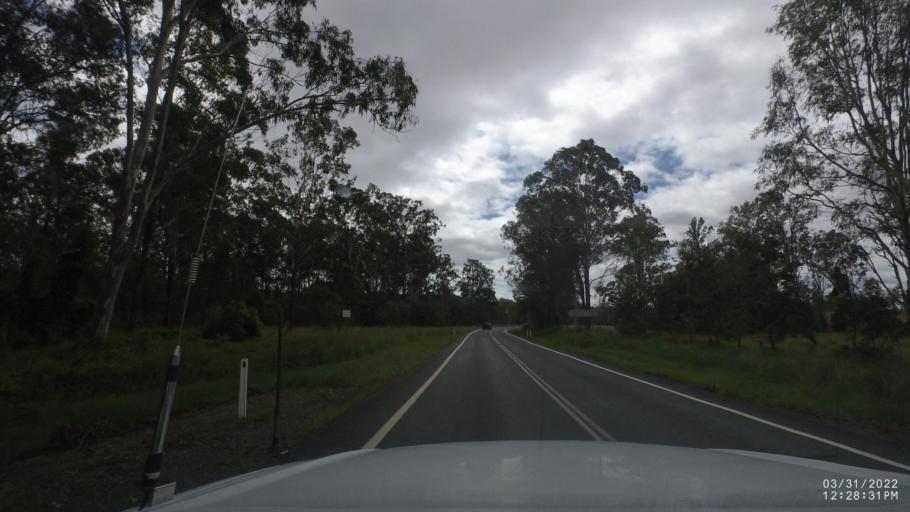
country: AU
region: Queensland
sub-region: Logan
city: Cedar Vale
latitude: -27.9316
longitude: 153.0797
